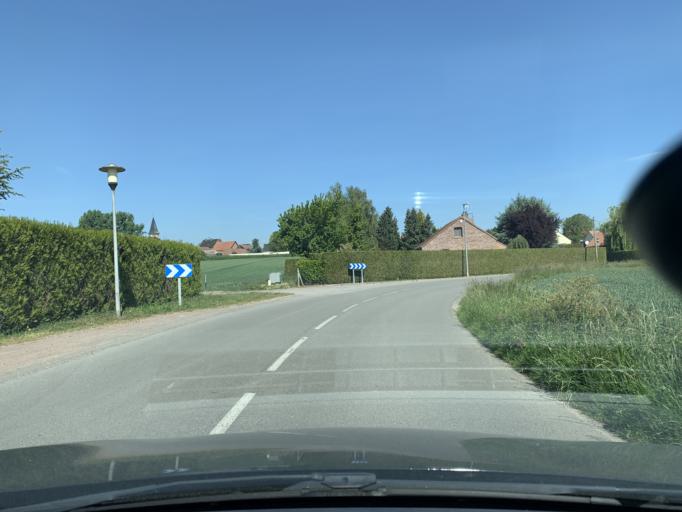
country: FR
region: Nord-Pas-de-Calais
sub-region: Departement du Nord
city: Fontaine-Notre-Dame
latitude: 50.1463
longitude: 3.1665
